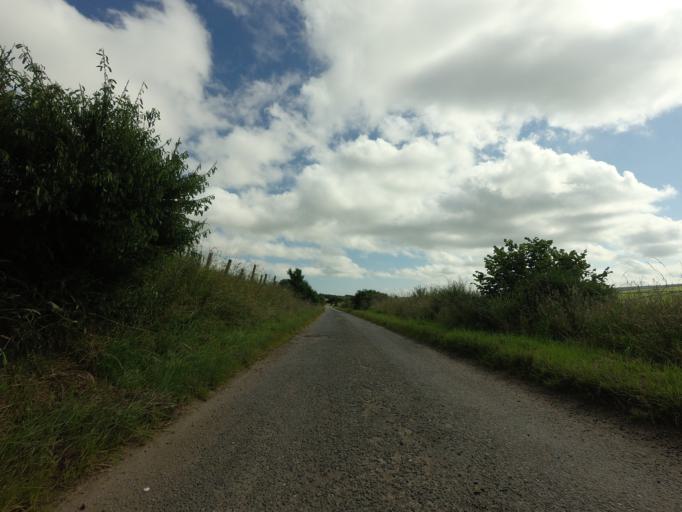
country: GB
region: Scotland
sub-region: Aberdeenshire
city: Banff
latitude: 57.6030
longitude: -2.5126
